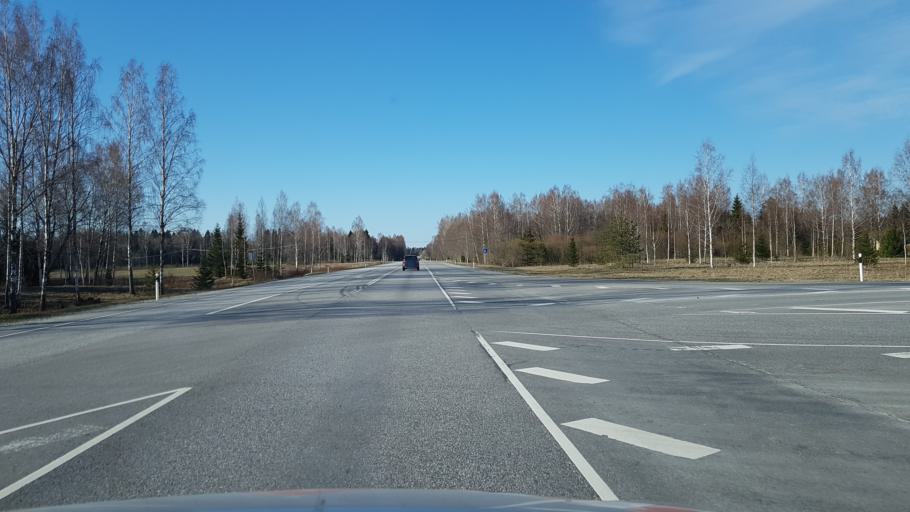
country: EE
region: Ida-Virumaa
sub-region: Johvi vald
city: Johvi
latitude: 59.1890
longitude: 27.3470
